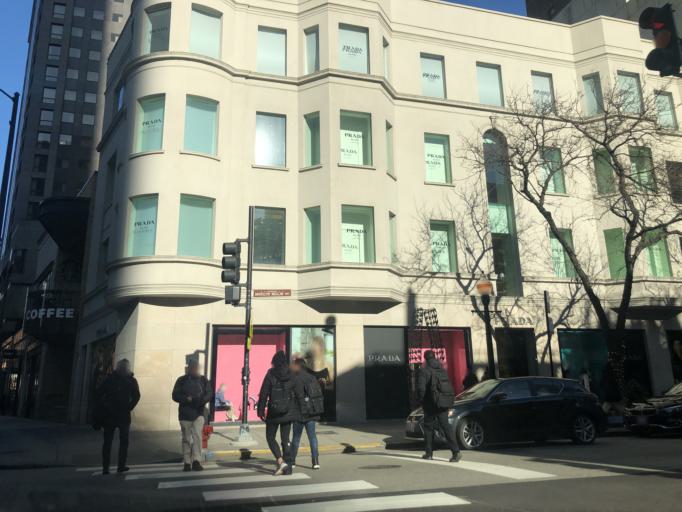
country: US
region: Illinois
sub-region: Cook County
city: Chicago
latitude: 41.9007
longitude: -87.6274
